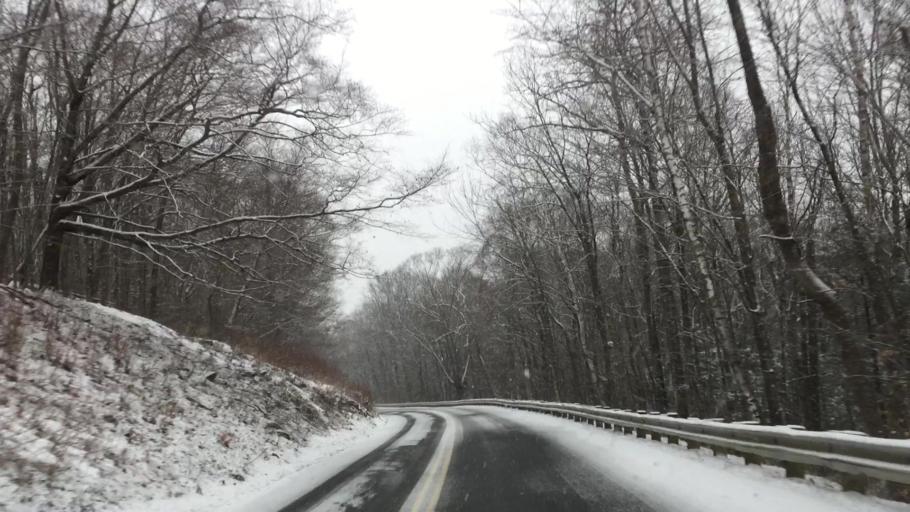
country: US
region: Massachusetts
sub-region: Berkshire County
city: Dalton
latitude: 42.4160
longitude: -73.1826
